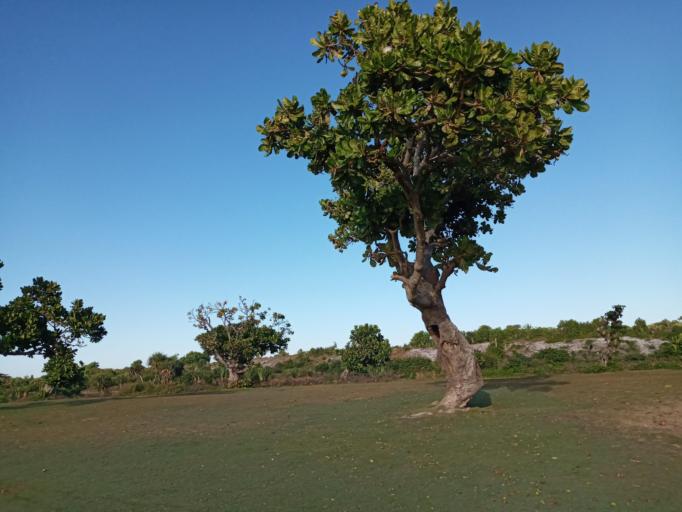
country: MG
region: Atsimo-Atsinanana
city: Vohipaho
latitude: -23.5590
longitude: 47.6281
